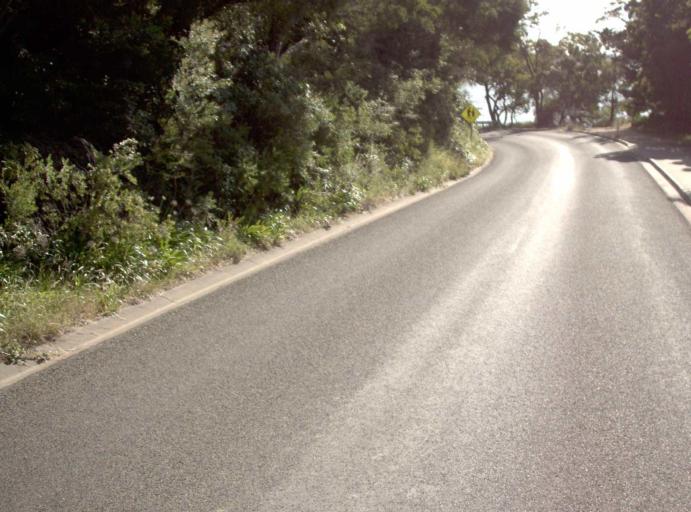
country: AU
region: Victoria
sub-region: East Gippsland
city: Lakes Entrance
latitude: -37.8902
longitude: 147.8545
